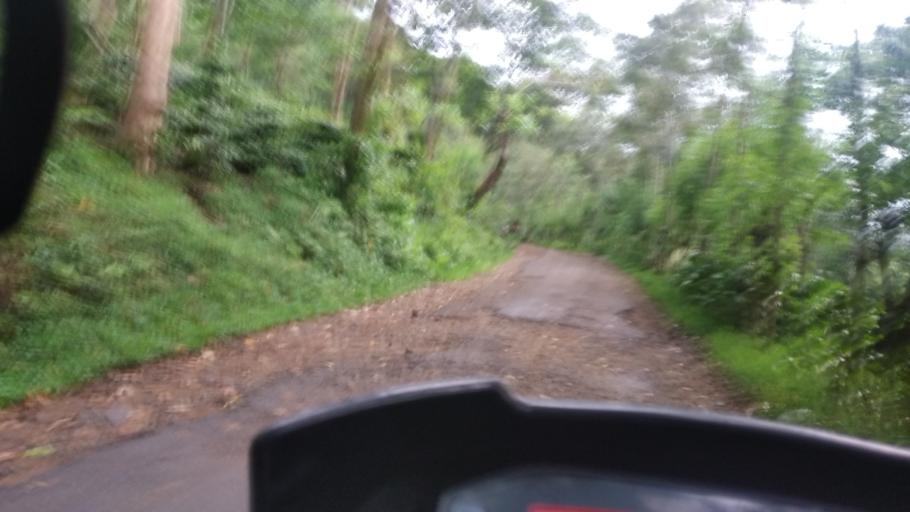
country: IN
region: Tamil Nadu
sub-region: Theni
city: Gudalur
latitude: 9.5544
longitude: 77.0656
